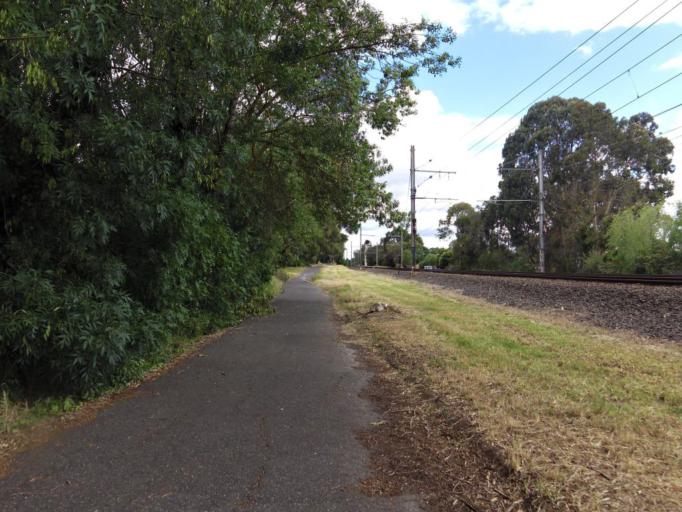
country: AU
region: Victoria
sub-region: Maroondah
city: Ringwood East
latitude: -37.8226
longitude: 145.2415
